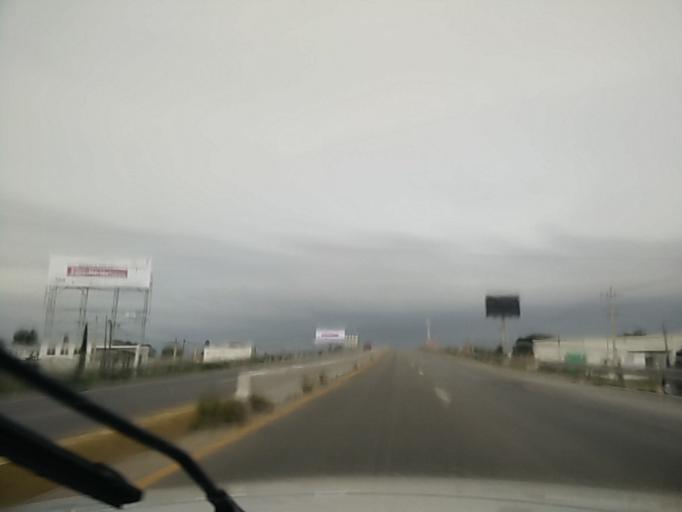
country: MX
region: Yucatan
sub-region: Kanasin
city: Kanasin
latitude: 20.9479
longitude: -89.5564
